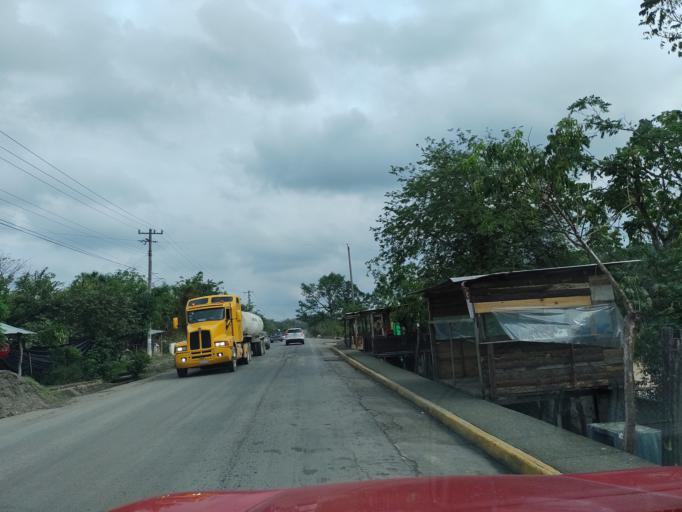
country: MX
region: Veracruz
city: Coatzintla
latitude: 20.4587
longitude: -97.4196
